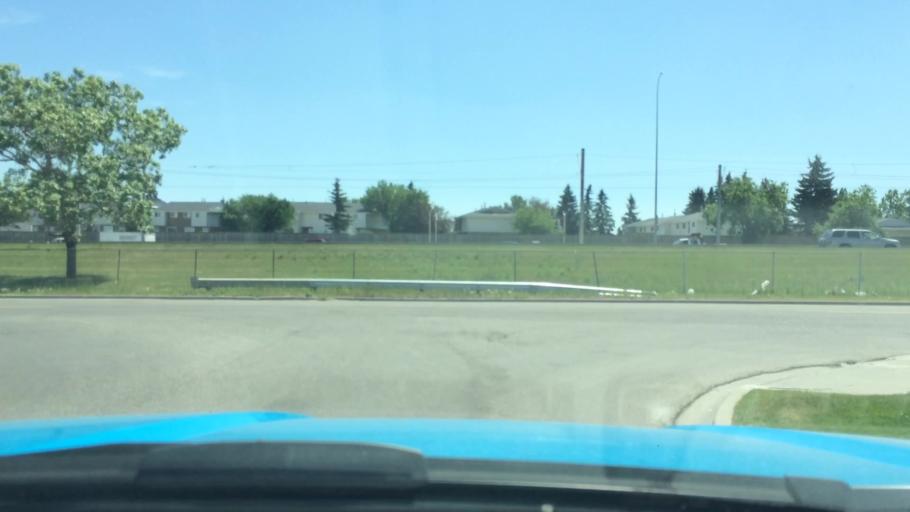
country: CA
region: Alberta
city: Calgary
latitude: 51.0510
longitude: -113.9890
